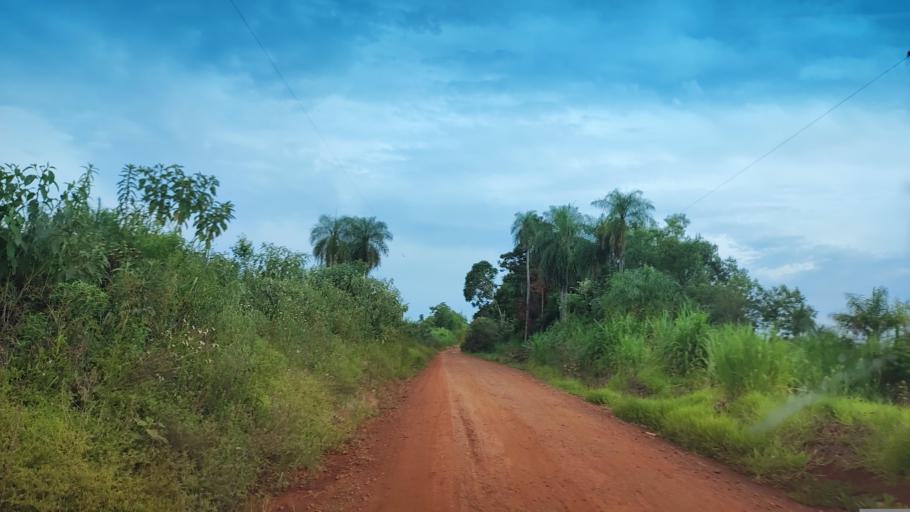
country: AR
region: Misiones
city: Gobernador Roca
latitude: -27.1607
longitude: -55.4607
